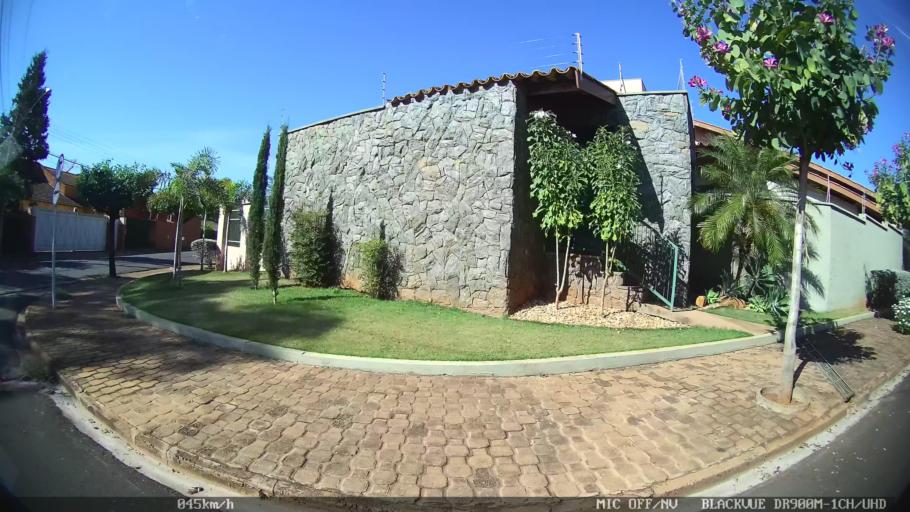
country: BR
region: Sao Paulo
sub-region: Olimpia
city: Olimpia
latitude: -20.7327
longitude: -48.9179
